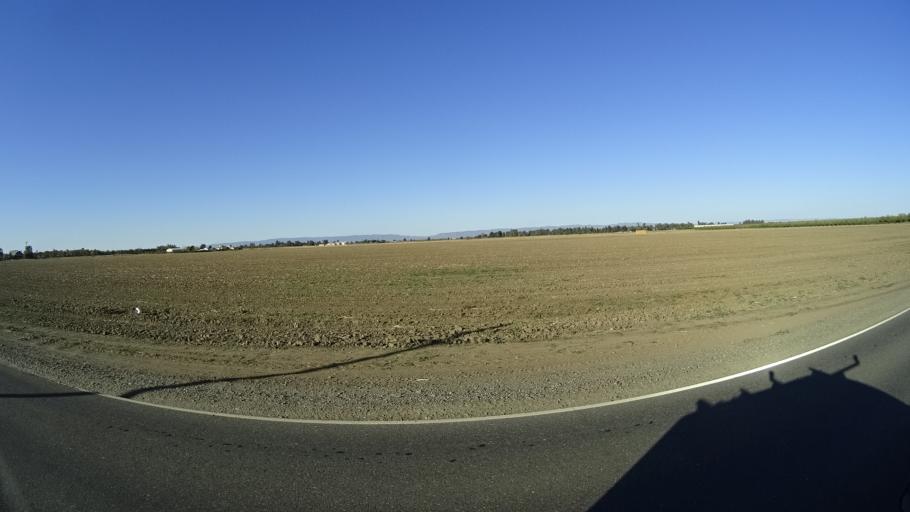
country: US
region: California
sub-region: Yolo County
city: Davis
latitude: 38.5845
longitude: -121.7507
